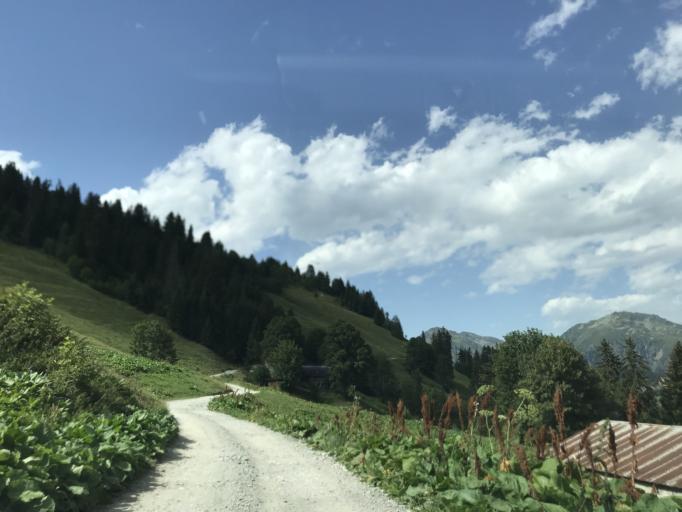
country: FR
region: Rhone-Alpes
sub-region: Departement de la Savoie
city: Beaufort
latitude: 45.6679
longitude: 6.6144
